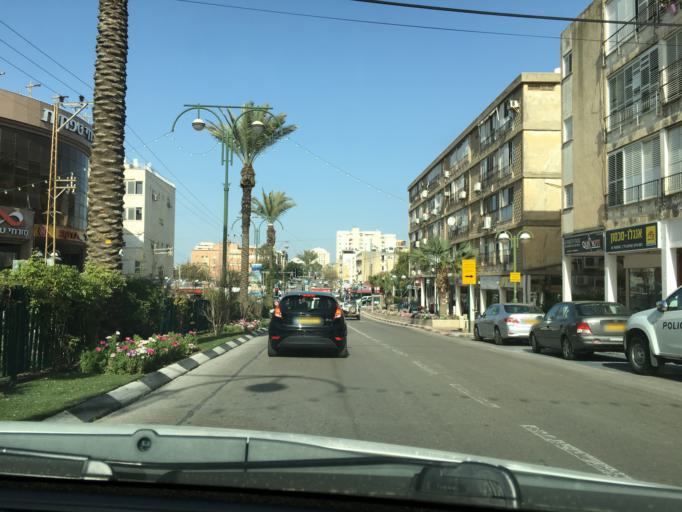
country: IL
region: Tel Aviv
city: Ramat HaSharon
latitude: 32.1450
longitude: 34.8383
